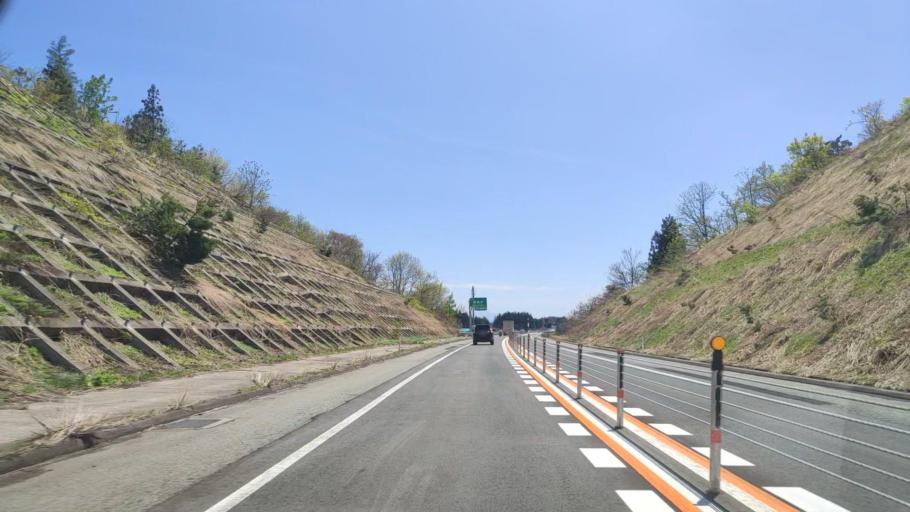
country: JP
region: Yamagata
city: Obanazawa
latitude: 38.6429
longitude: 140.3734
